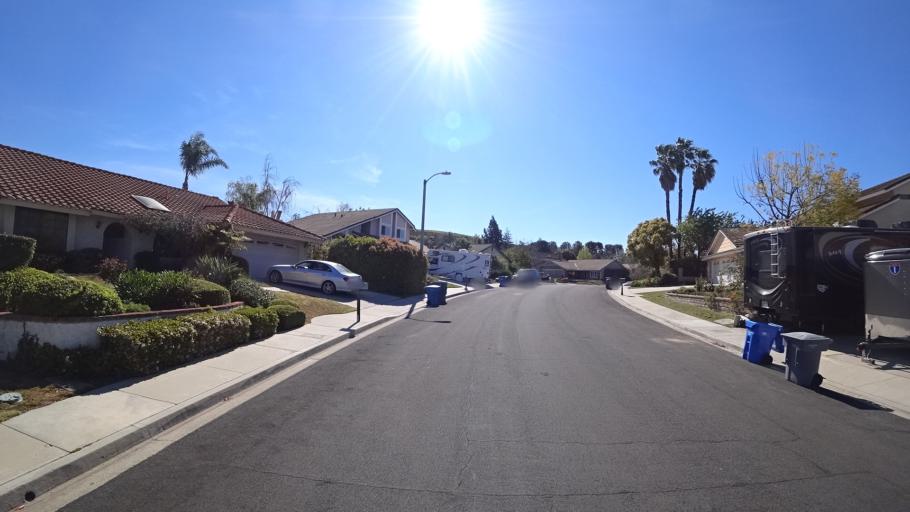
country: US
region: California
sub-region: Ventura County
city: Thousand Oaks
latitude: 34.2267
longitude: -118.8589
